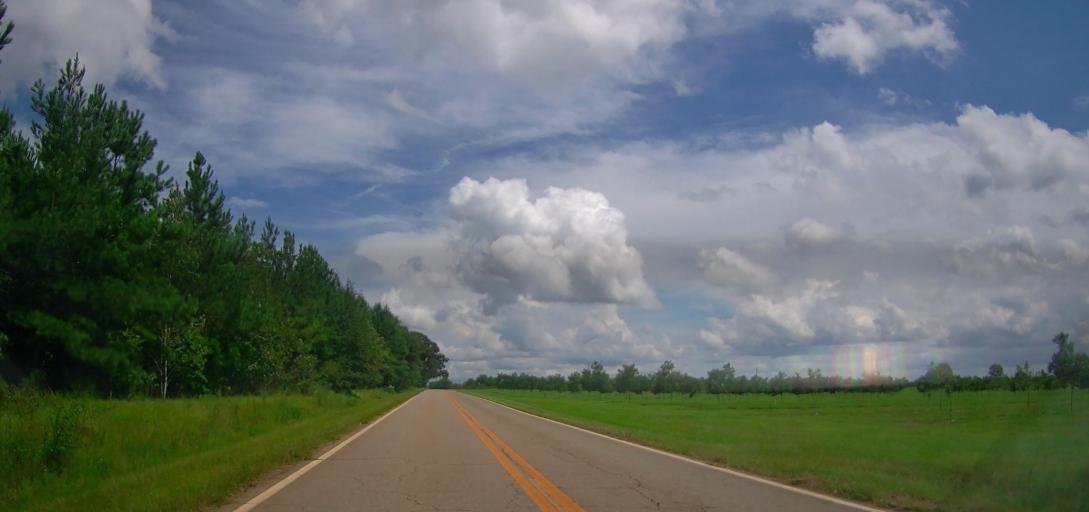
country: US
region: Georgia
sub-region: Peach County
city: Fort Valley
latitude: 32.5332
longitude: -83.8058
